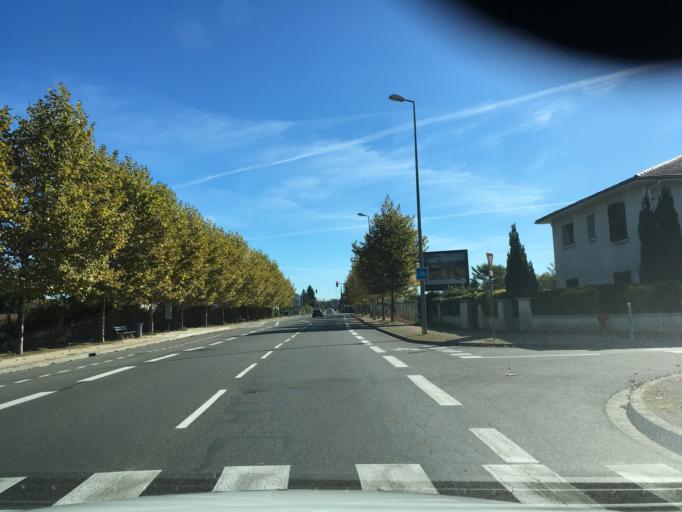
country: FR
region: Aquitaine
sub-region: Departement des Pyrenees-Atlantiques
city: Pau
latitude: 43.3170
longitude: -0.3414
